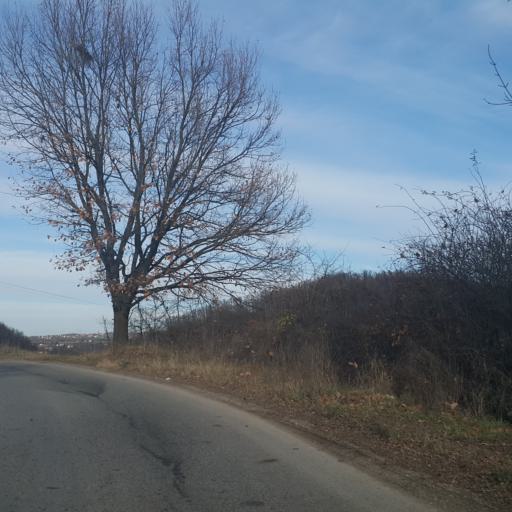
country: RS
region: Central Serbia
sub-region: Belgrade
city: Lazarevac
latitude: 44.3534
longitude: 20.4028
